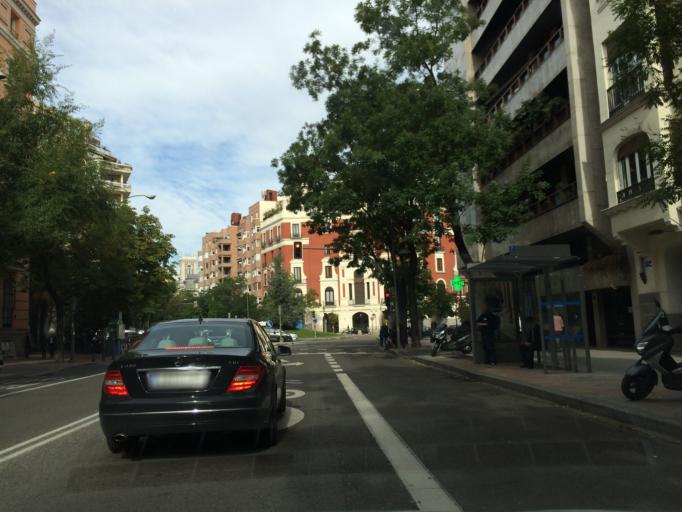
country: ES
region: Madrid
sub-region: Provincia de Madrid
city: Salamanca
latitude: 40.4323
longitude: -3.6916
